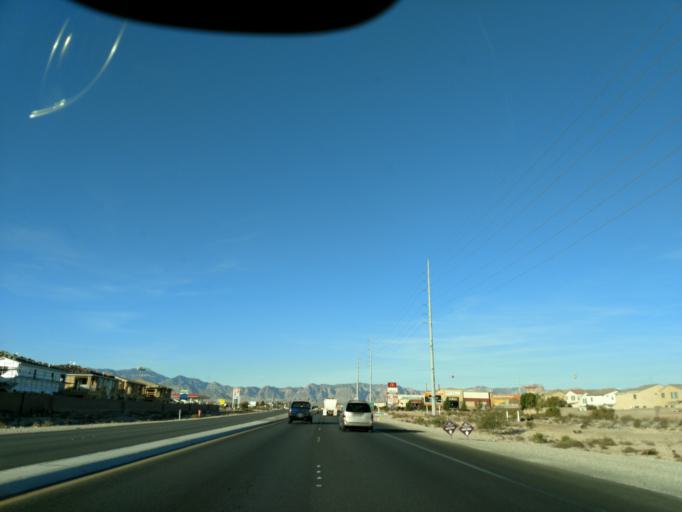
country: US
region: Nevada
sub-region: Clark County
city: Enterprise
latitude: 36.0203
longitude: -115.2745
